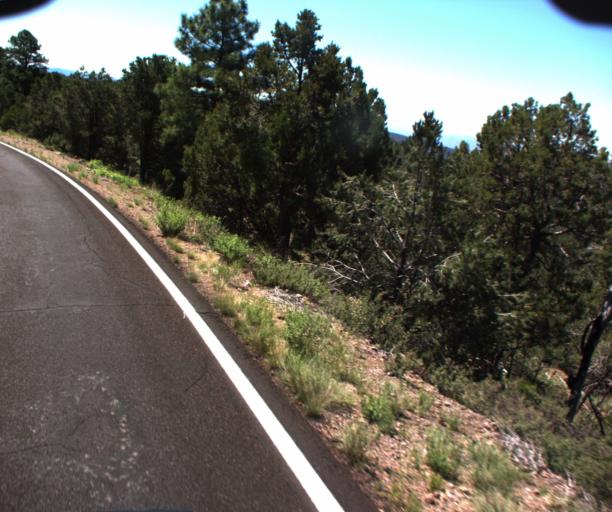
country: US
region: Arizona
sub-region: Greenlee County
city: Morenci
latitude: 33.4227
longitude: -109.3725
